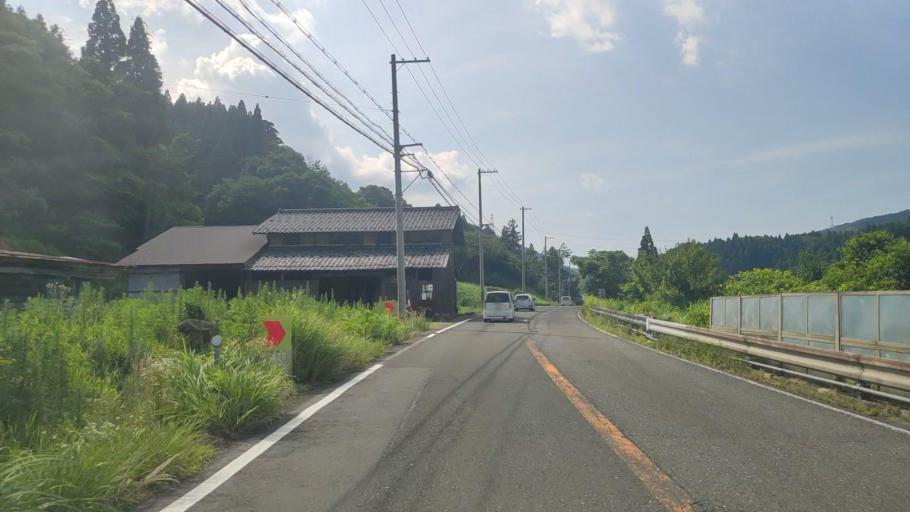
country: JP
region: Fukui
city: Tsuruga
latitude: 35.5526
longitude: 136.1416
